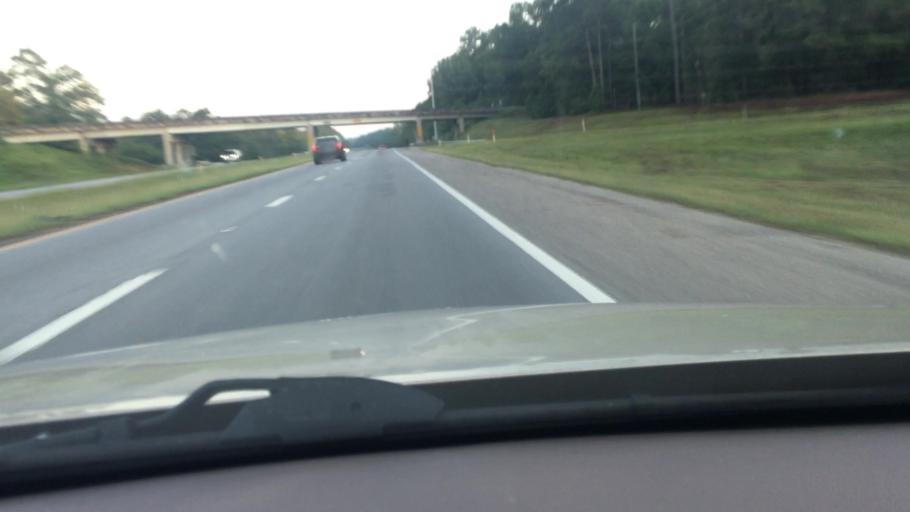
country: US
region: South Carolina
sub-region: Richland County
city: Lake Murray of Richland
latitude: 34.1454
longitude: -81.2365
